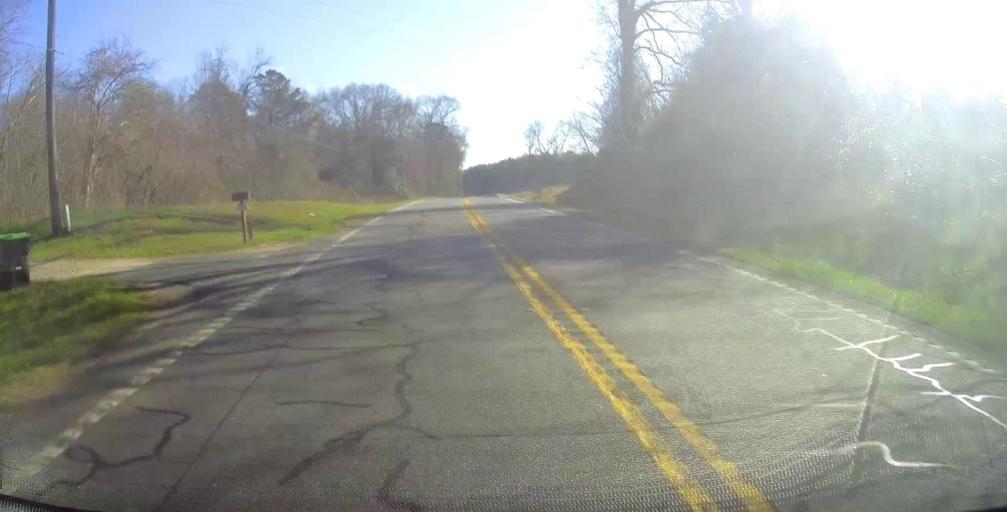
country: US
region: Georgia
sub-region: Talbot County
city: Sardis
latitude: 32.7705
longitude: -84.5578
